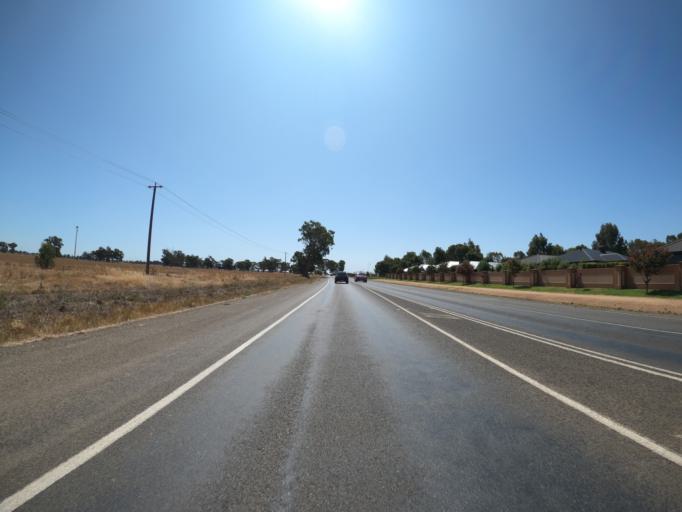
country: AU
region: Victoria
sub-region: Moira
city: Yarrawonga
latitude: -36.0119
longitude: 146.0361
